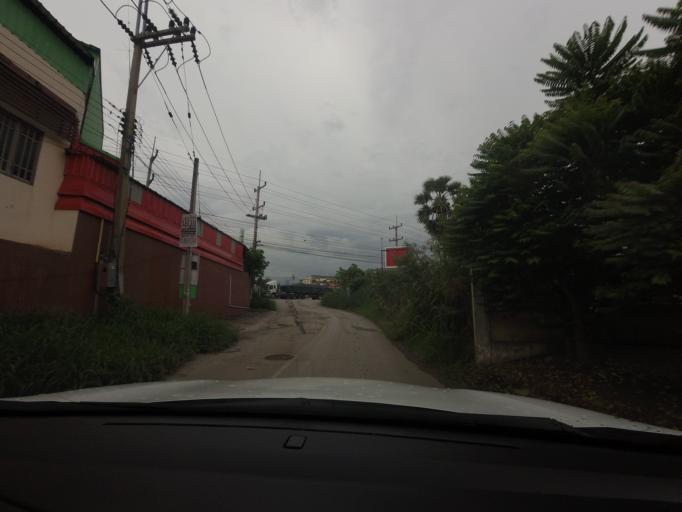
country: TH
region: Nakhon Ratchasima
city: Pak Chong
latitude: 14.6654
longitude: 101.4274
